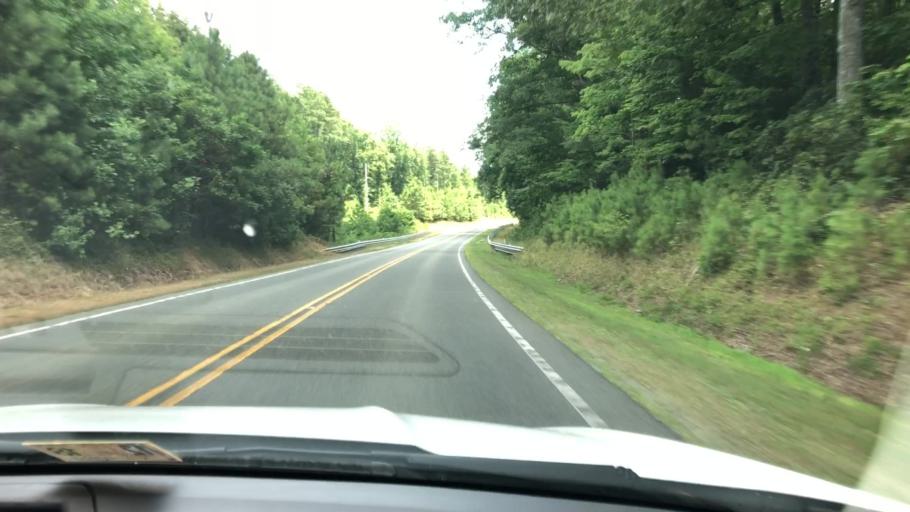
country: US
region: Virginia
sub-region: Lancaster County
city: Lancaster
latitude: 37.8265
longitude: -76.5634
